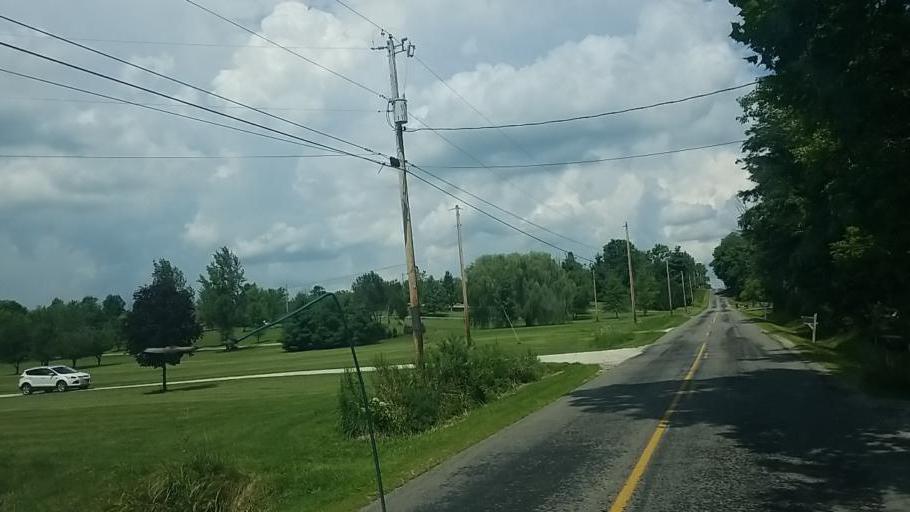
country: US
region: Ohio
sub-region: Medina County
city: Lodi
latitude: 41.1038
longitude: -82.0752
